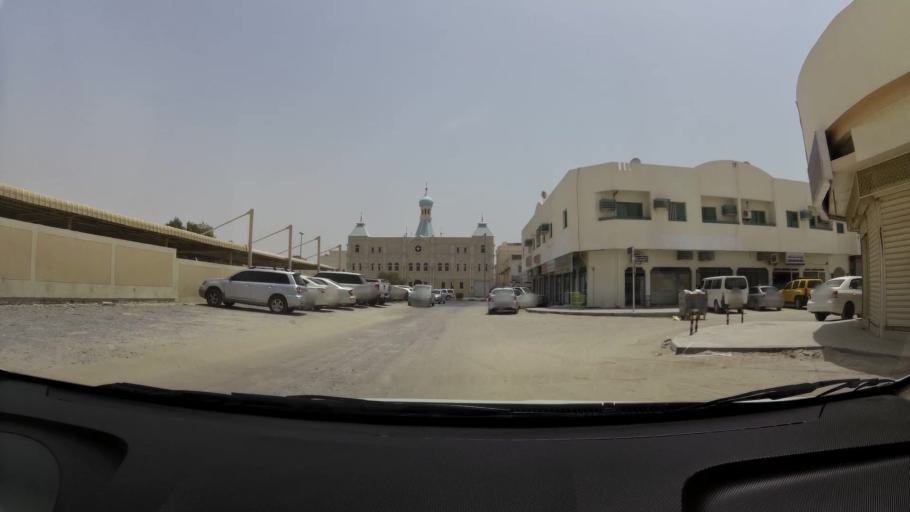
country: AE
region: Ash Shariqah
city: Sharjah
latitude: 25.3511
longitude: 55.4046
